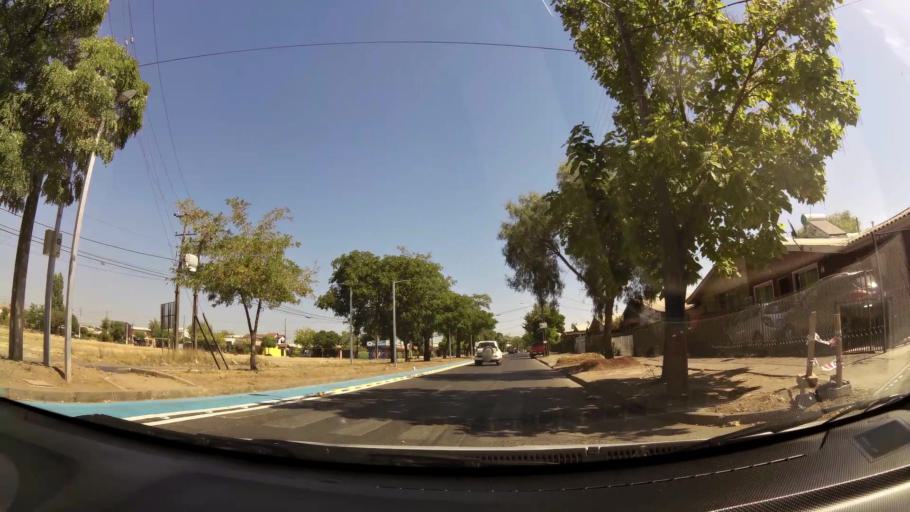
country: CL
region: Maule
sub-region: Provincia de Talca
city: Talca
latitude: -35.4430
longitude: -71.6533
